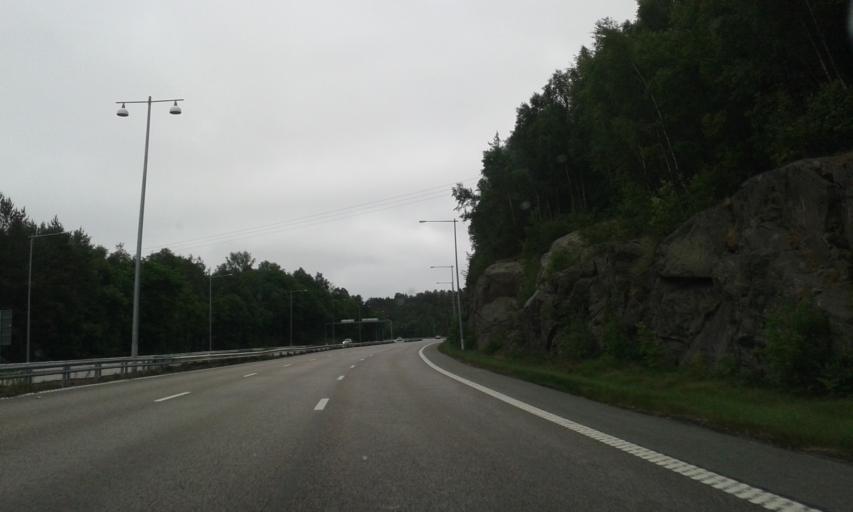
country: SE
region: Vaestra Goetaland
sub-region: Goteborg
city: Hammarkullen
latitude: 57.7881
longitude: 12.0206
